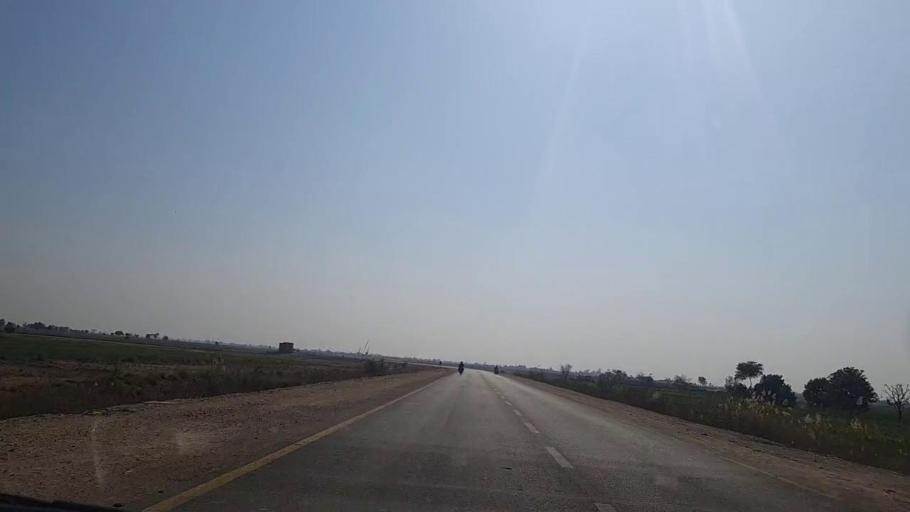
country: PK
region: Sindh
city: Sakrand
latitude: 26.0892
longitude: 68.4016
